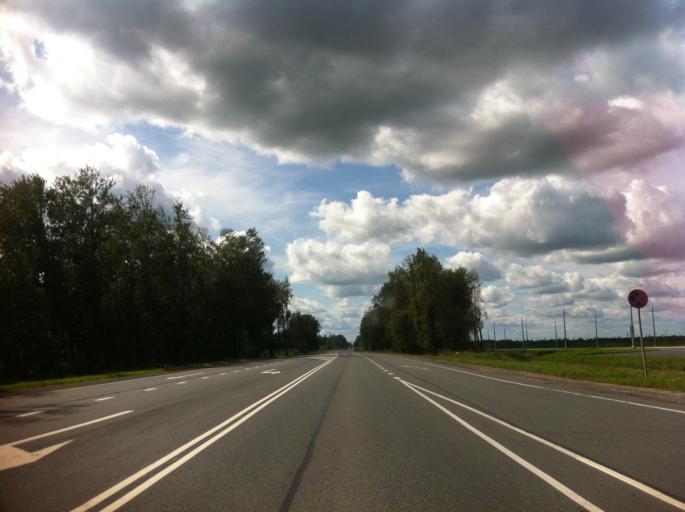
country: RU
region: Pskov
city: Pskov
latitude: 57.7738
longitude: 28.1391
